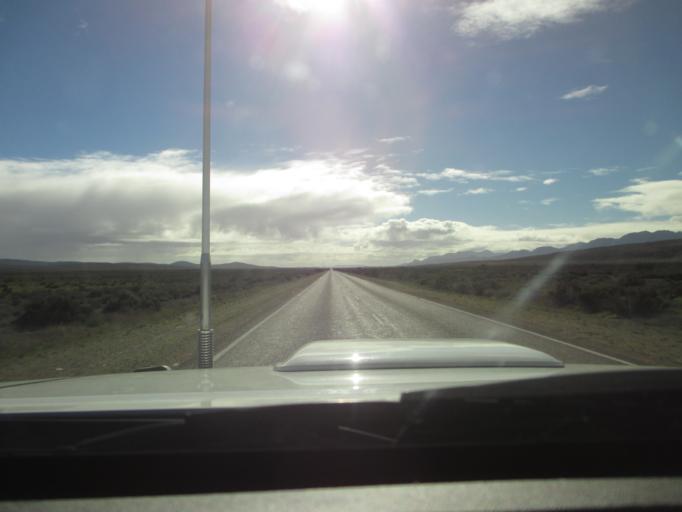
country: AU
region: South Australia
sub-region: Flinders Ranges
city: Quorn
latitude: -31.7316
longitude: 138.3427
